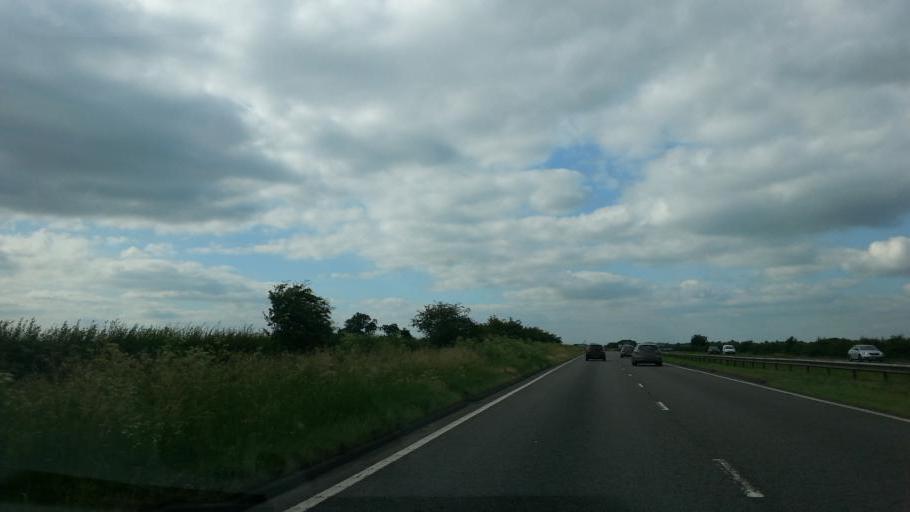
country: GB
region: England
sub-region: Lincolnshire
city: Long Bennington
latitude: 53.0172
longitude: -0.7657
